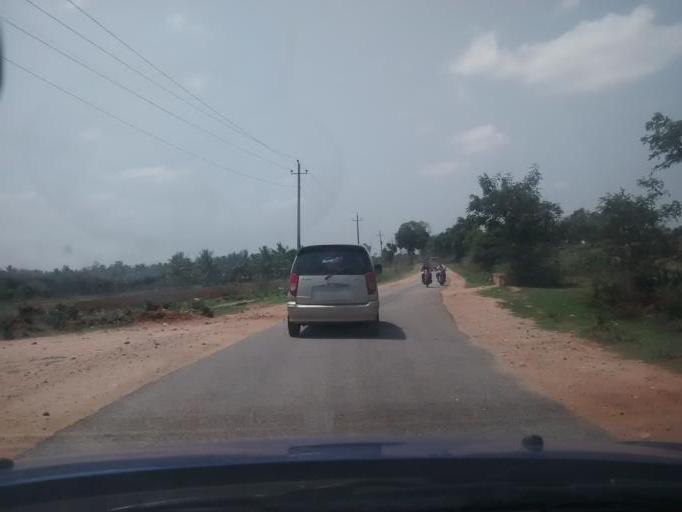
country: IN
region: Karnataka
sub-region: Hassan
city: Konanur
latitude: 12.5763
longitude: 76.2290
